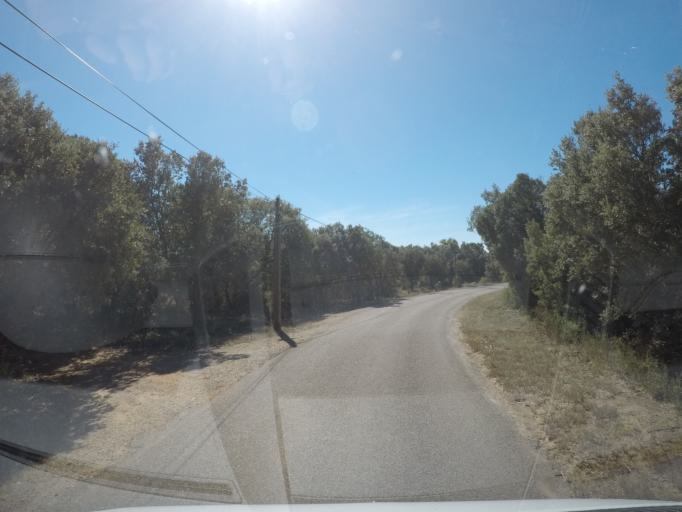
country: FR
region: Languedoc-Roussillon
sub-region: Departement de l'Herault
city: Aniane
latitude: 43.7312
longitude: 3.6507
